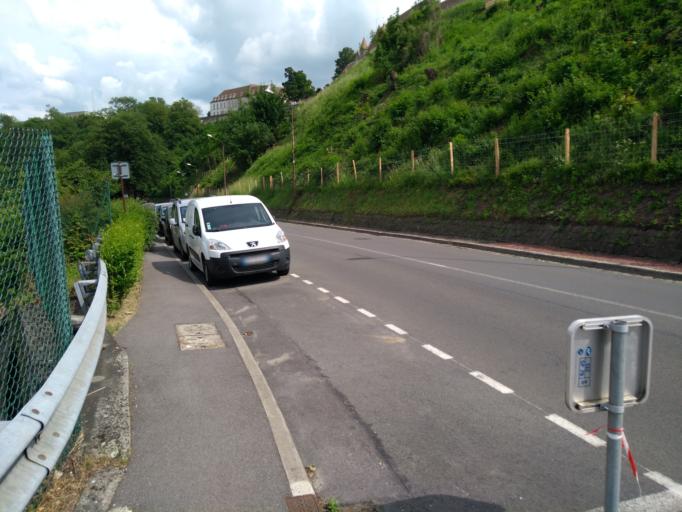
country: FR
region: Picardie
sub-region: Departement de l'Aisne
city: Laon
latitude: 49.5657
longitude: 3.6244
